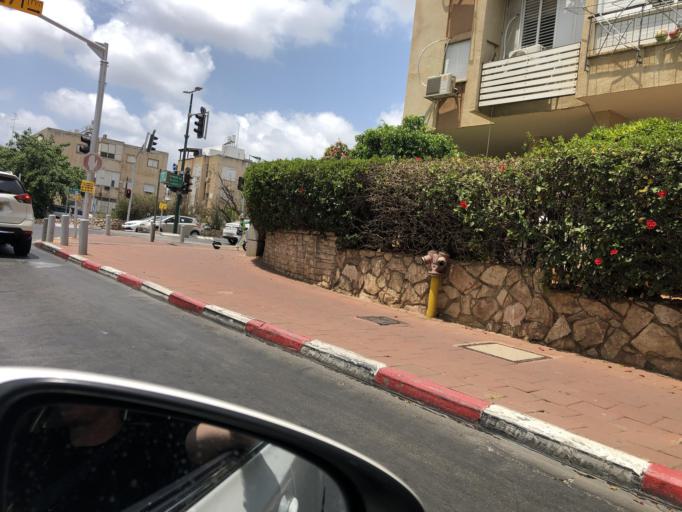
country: IL
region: Tel Aviv
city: Giv`atayim
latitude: 32.0615
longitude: 34.8289
